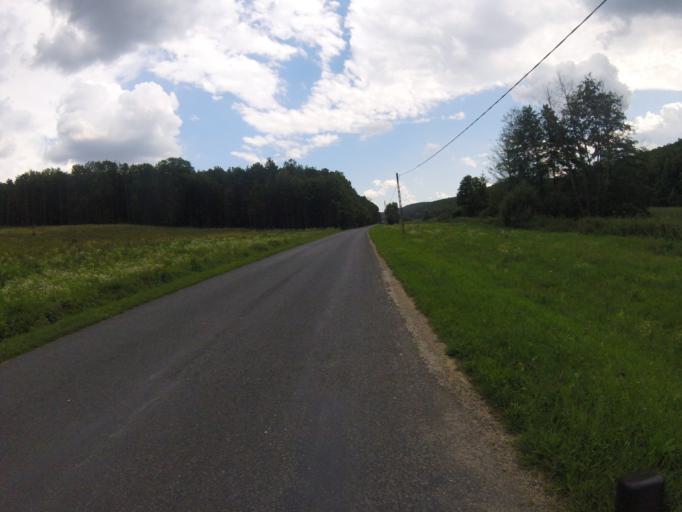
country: HU
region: Zala
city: Becsehely
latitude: 46.4998
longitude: 16.7395
